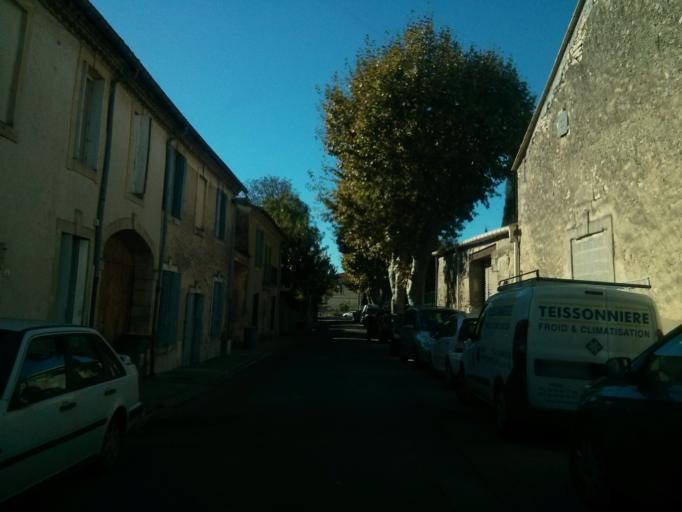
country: FR
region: Languedoc-Roussillon
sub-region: Departement du Gard
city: Congenies
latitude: 43.7770
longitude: 4.1603
